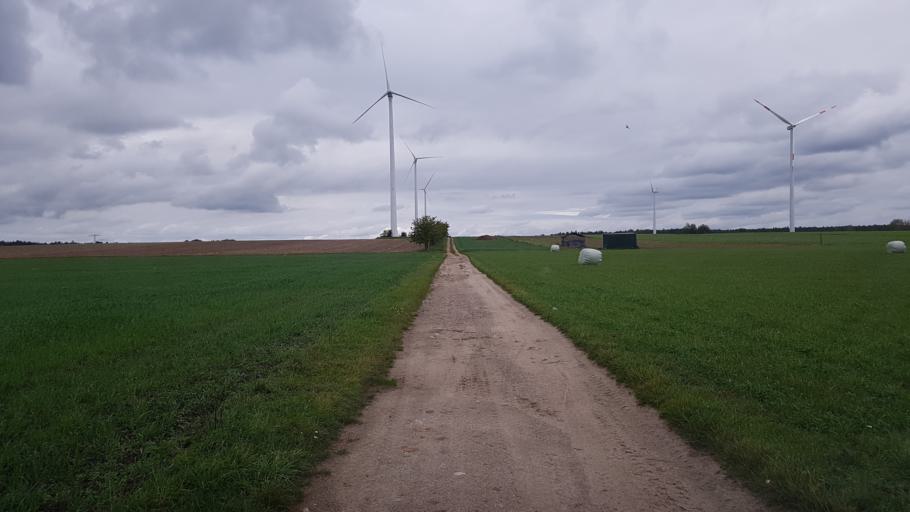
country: DE
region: Brandenburg
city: Doberlug-Kirchhain
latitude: 51.6142
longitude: 13.5921
